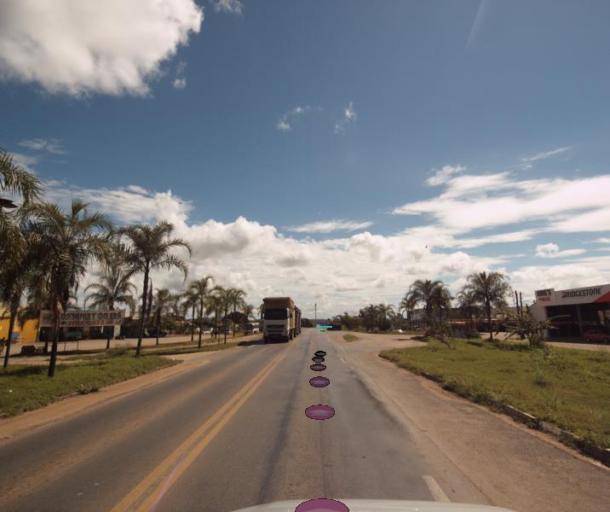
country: BR
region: Goias
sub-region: Uruacu
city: Uruacu
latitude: -14.5267
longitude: -49.1595
